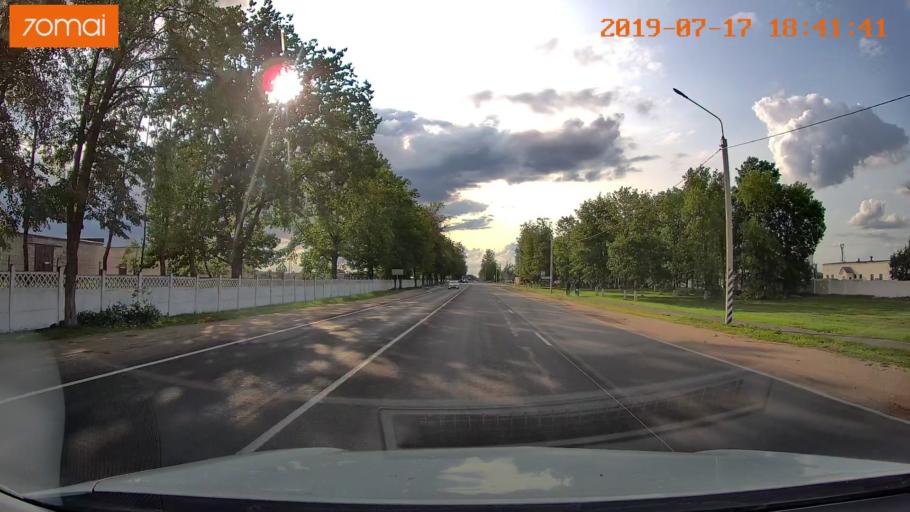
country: BY
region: Mogilev
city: Asipovichy
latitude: 53.3069
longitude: 28.6576
